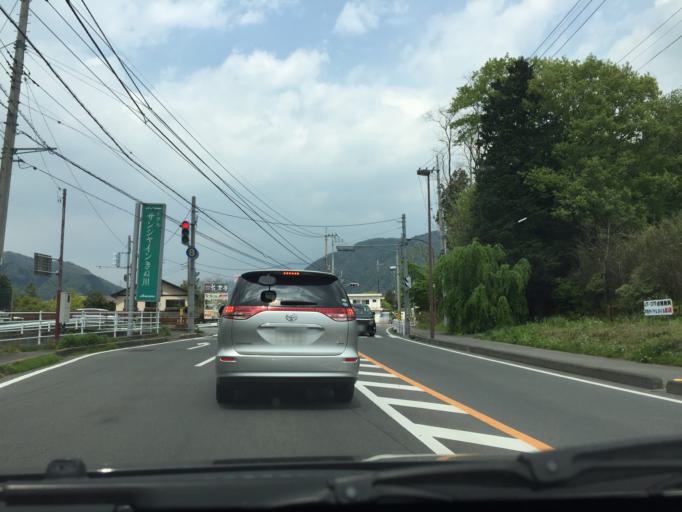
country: JP
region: Tochigi
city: Imaichi
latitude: 36.8119
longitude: 139.7108
